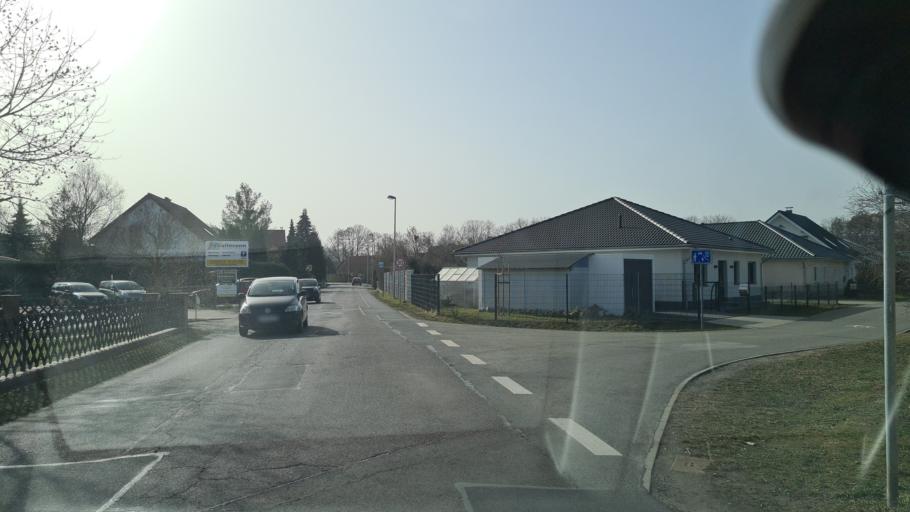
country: DE
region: Brandenburg
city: Cottbus
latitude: 51.7342
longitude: 14.3634
